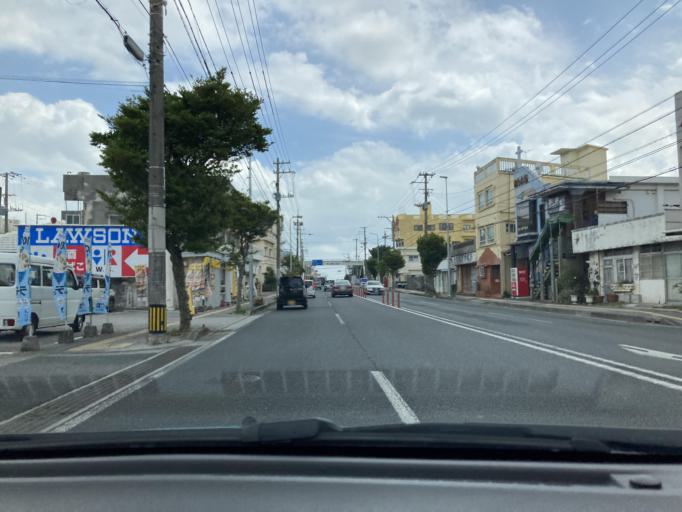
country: JP
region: Okinawa
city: Okinawa
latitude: 26.3343
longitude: 127.8186
